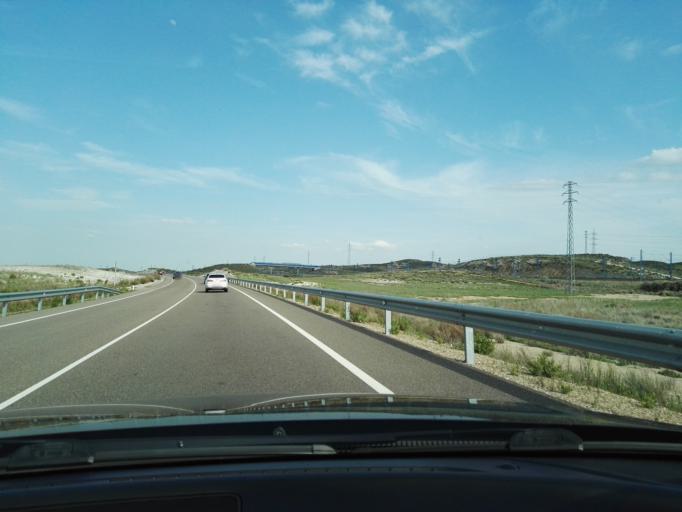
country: ES
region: Aragon
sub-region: Provincia de Zaragoza
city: Montecanal
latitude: 41.6227
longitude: -0.9816
